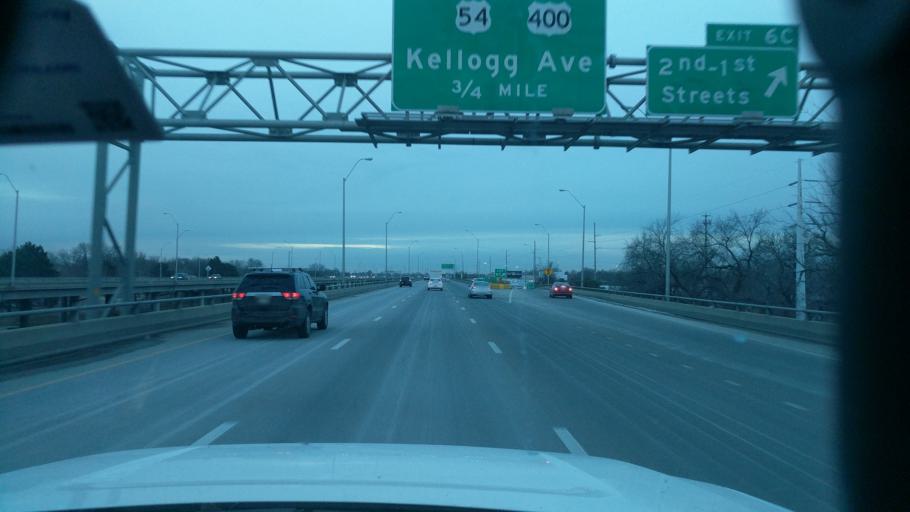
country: US
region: Kansas
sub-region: Sedgwick County
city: Wichita
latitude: 37.6927
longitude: -97.3155
